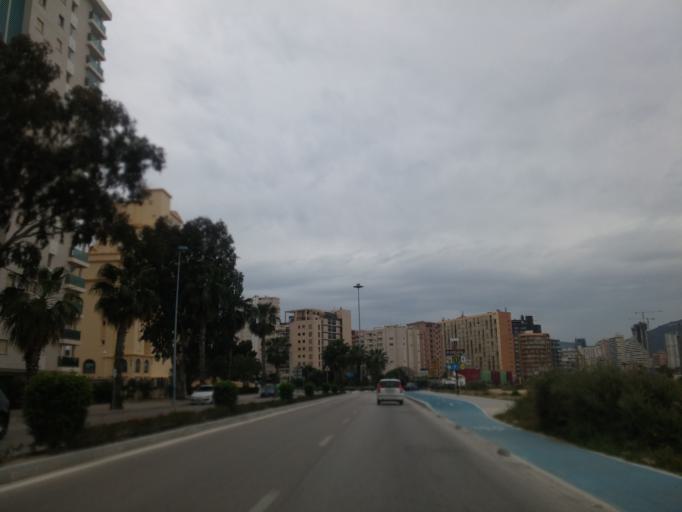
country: ES
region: Valencia
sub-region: Provincia de Alicante
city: Calp
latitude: 38.6426
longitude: 0.0677
